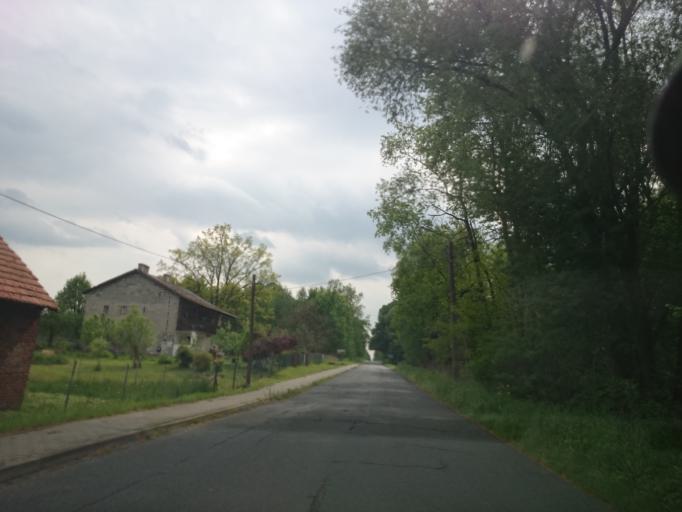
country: PL
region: Lower Silesian Voivodeship
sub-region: Powiat olesnicki
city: Dobroszyce
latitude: 51.3579
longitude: 17.2817
